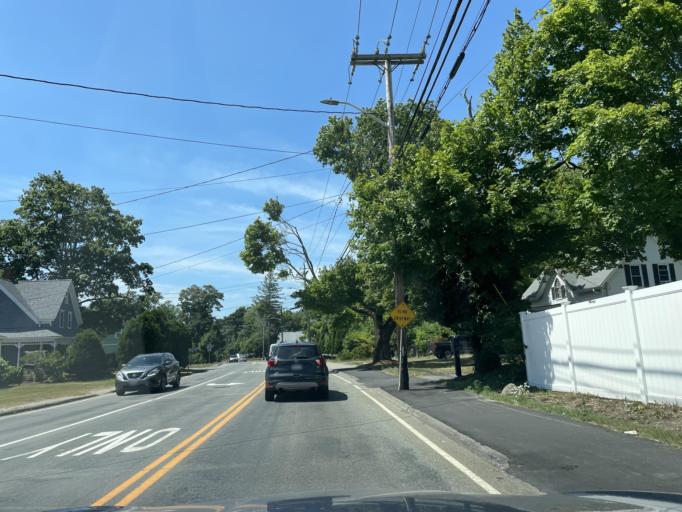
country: US
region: Massachusetts
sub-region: Norfolk County
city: Stoughton
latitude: 42.1334
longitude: -71.0920
